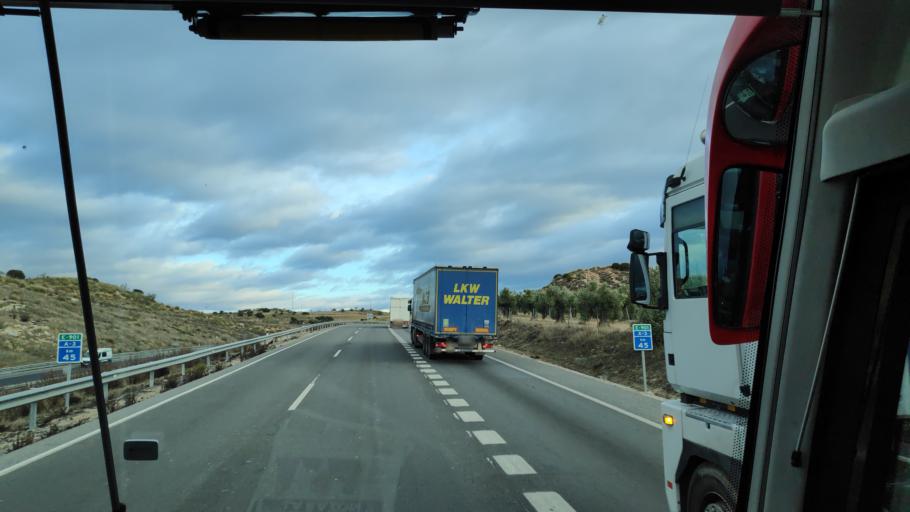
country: ES
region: Madrid
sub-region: Provincia de Madrid
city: Villarejo de Salvanes
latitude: 40.1980
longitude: -3.3099
